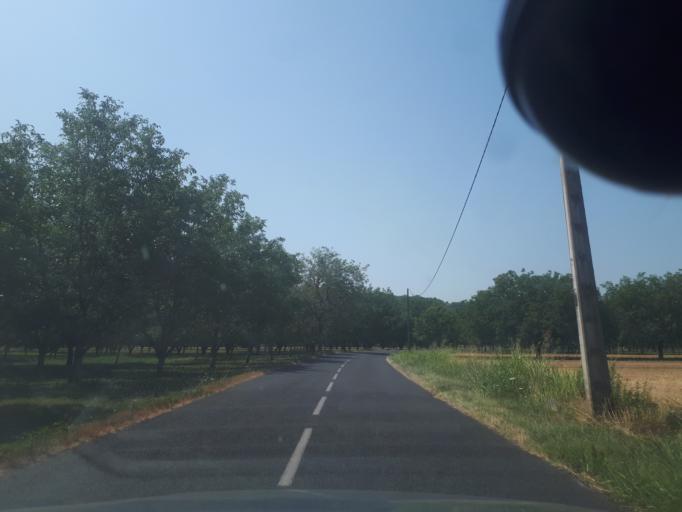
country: FR
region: Midi-Pyrenees
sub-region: Departement du Lot
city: Souillac
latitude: 44.8766
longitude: 1.4454
